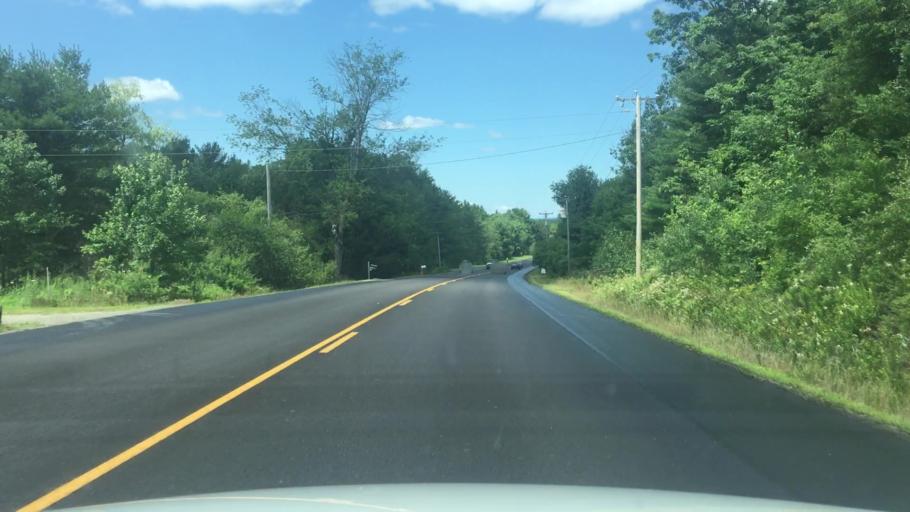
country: US
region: Maine
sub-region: Waldo County
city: Searsmont
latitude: 44.3996
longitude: -69.1568
